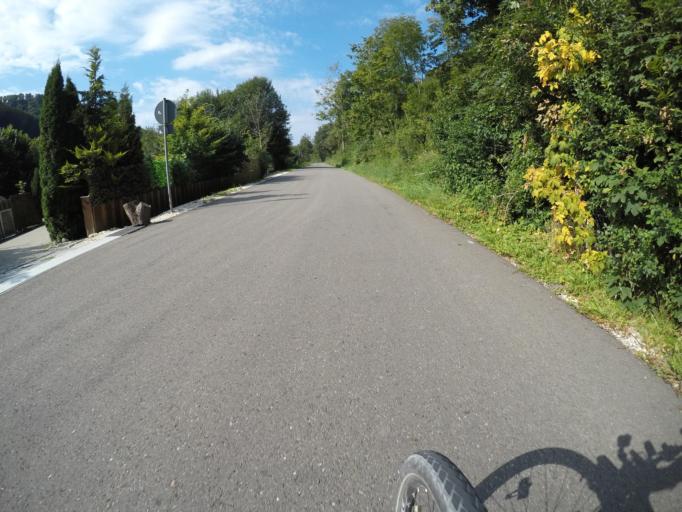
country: DE
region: Baden-Wuerttemberg
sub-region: Regierungsbezirk Stuttgart
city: Geislingen an der Steige
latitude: 48.6324
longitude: 9.8559
